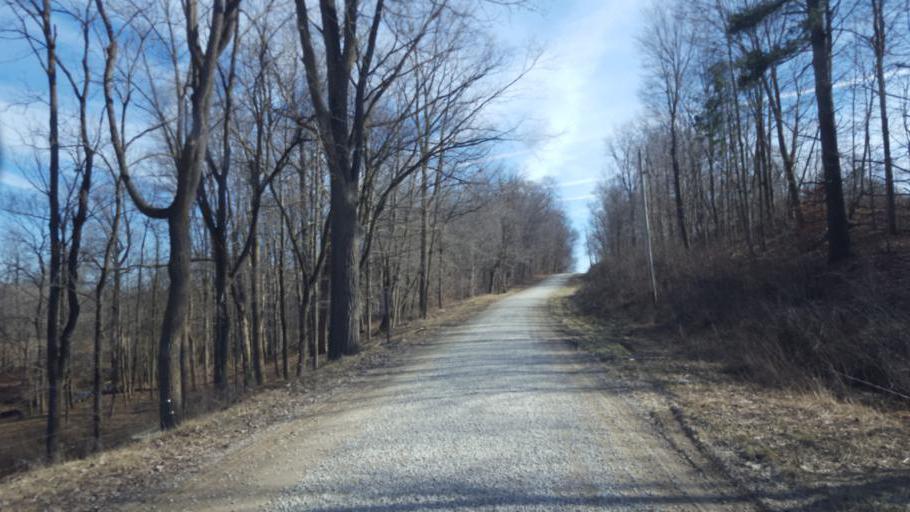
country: US
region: Ohio
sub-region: Richland County
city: Lexington
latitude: 40.5675
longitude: -82.6535
